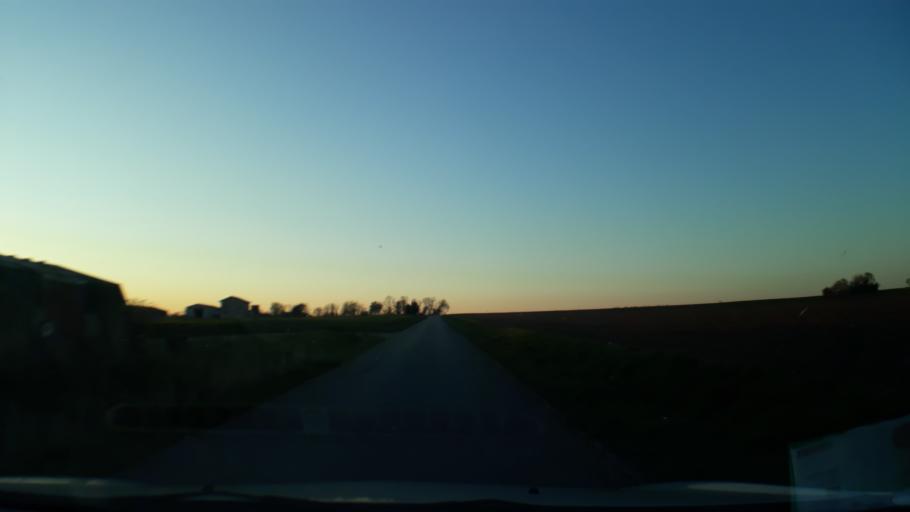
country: DE
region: North Rhine-Westphalia
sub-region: Regierungsbezirk Koln
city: Vettweiss
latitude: 50.7066
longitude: 6.6188
